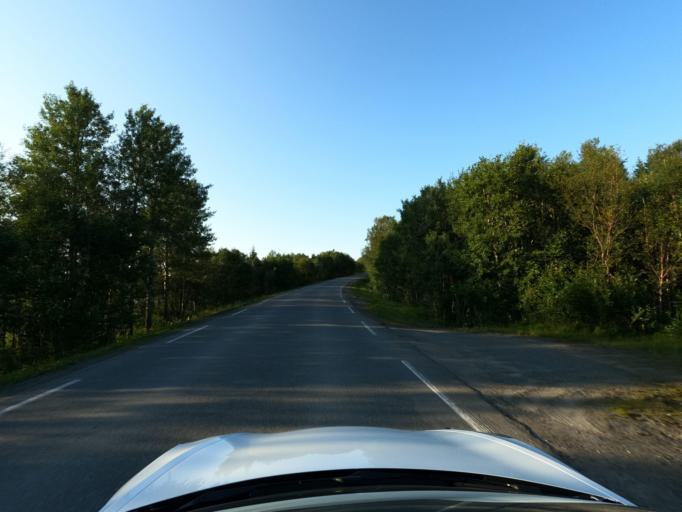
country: NO
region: Troms
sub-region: Skanland
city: Evenskjer
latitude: 68.4861
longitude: 16.7120
